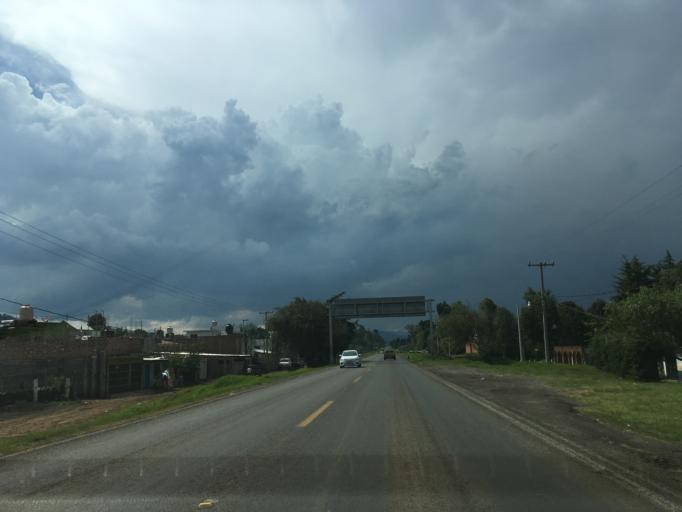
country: MX
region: Michoacan
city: Patzcuaro
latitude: 19.5323
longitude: -101.6218
